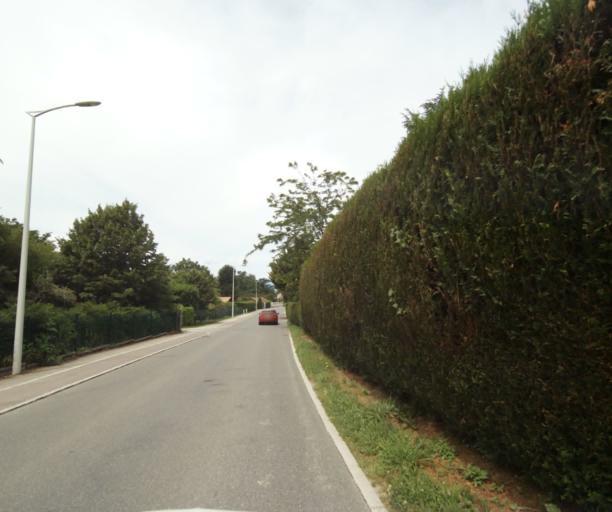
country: FR
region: Rhone-Alpes
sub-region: Departement de la Haute-Savoie
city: Anthy-sur-Leman
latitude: 46.3455
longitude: 6.4116
